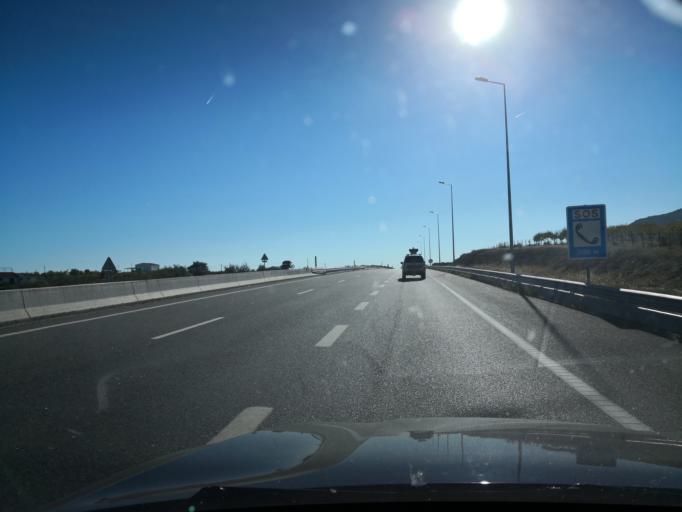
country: PT
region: Braganca
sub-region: Mirandela
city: Mirandela
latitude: 41.4754
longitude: -7.2243
